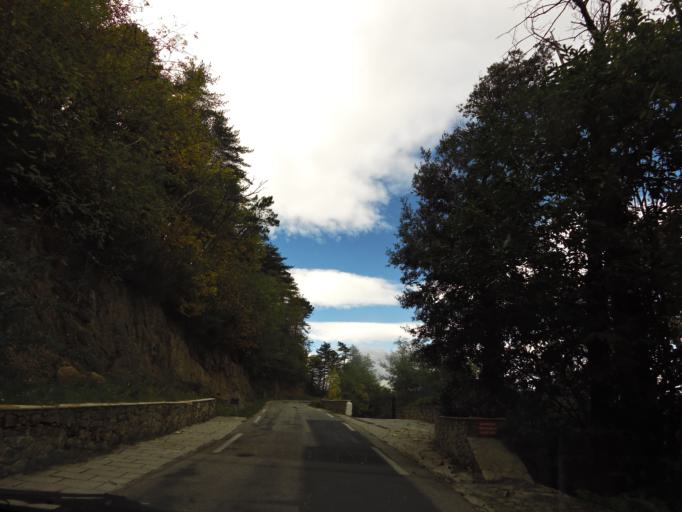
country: FR
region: Languedoc-Roussillon
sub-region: Departement du Gard
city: Lasalle
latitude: 44.0235
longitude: 3.8516
